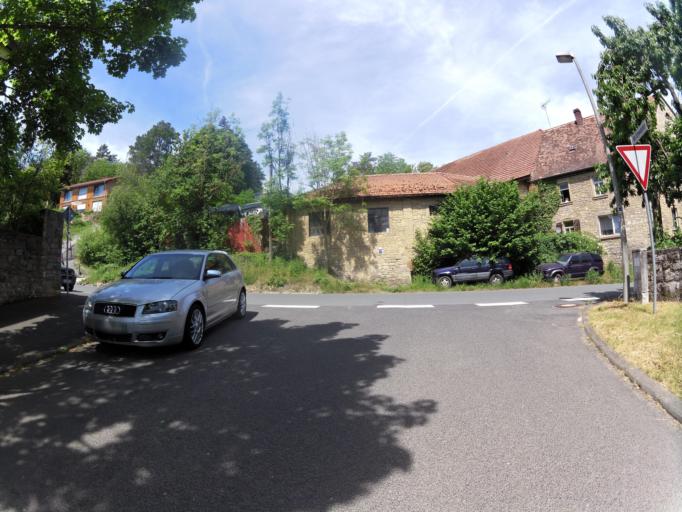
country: DE
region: Bavaria
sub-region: Regierungsbezirk Unterfranken
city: Sommerhausen
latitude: 49.6803
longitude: 10.0261
